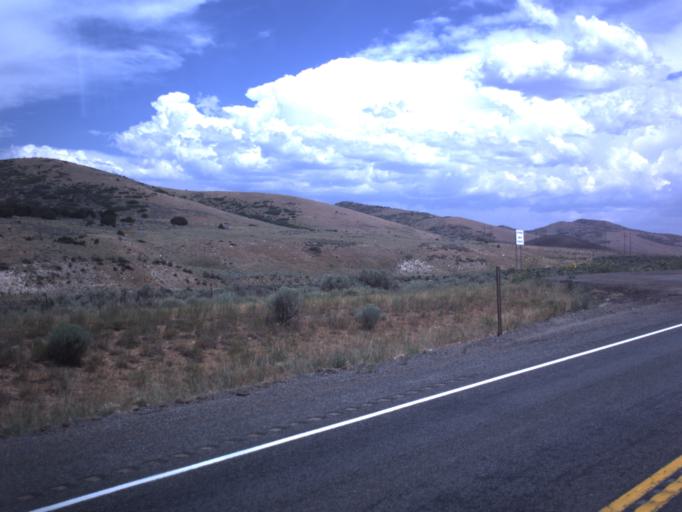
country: US
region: Utah
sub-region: Sanpete County
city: Fountain Green
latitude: 39.6945
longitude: -111.6909
